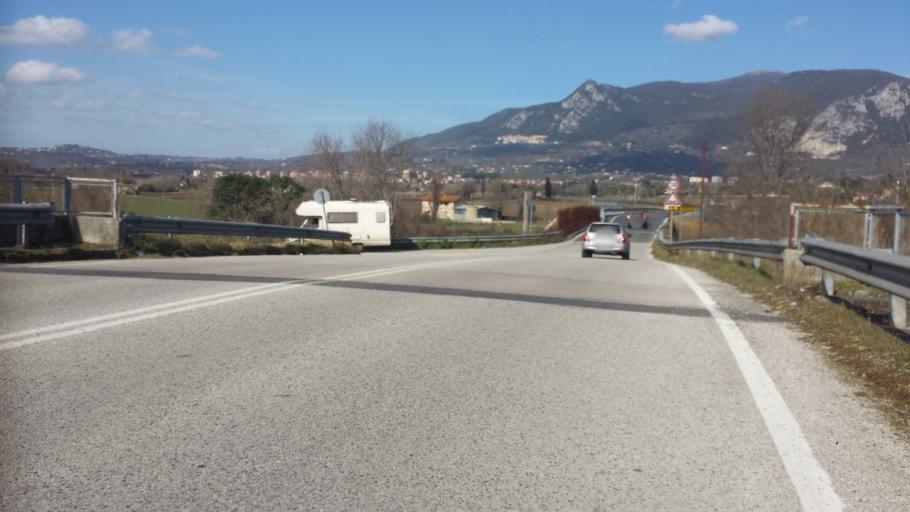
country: IT
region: Umbria
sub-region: Provincia di Terni
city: Terni
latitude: 42.5689
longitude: 12.5977
